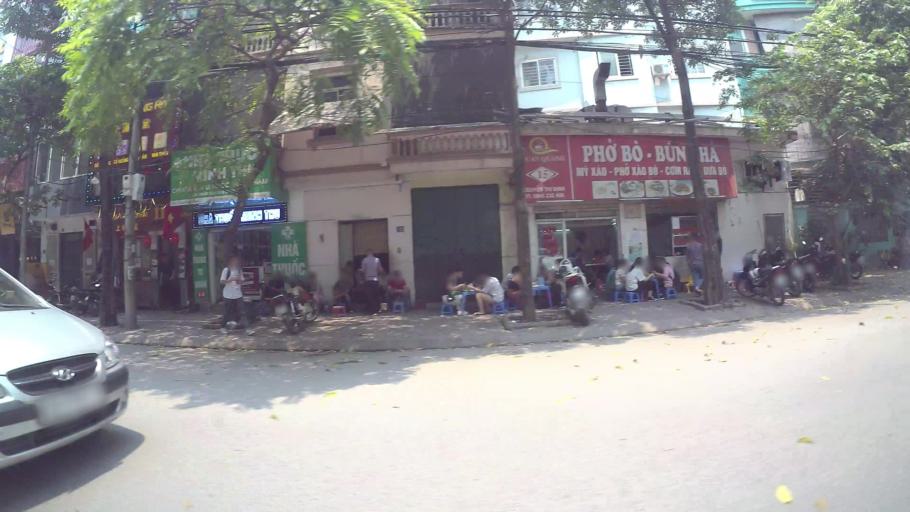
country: VN
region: Ha Noi
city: Thanh Xuan
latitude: 21.0124
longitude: 105.8038
